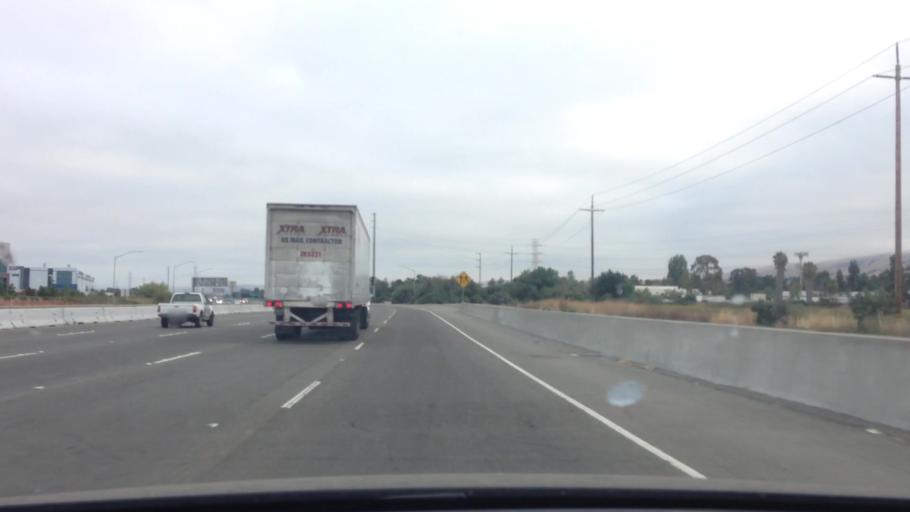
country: US
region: California
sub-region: Santa Clara County
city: Milpitas
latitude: 37.4563
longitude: -121.9230
